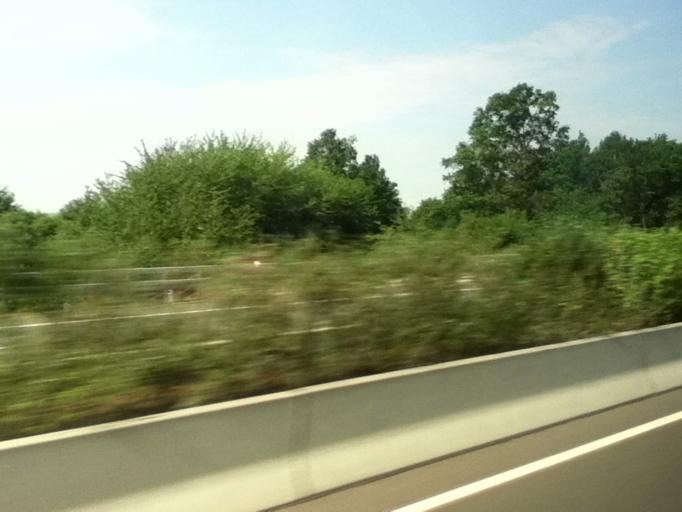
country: DE
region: Thuringia
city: Vollmershain
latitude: 50.8607
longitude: 12.3039
